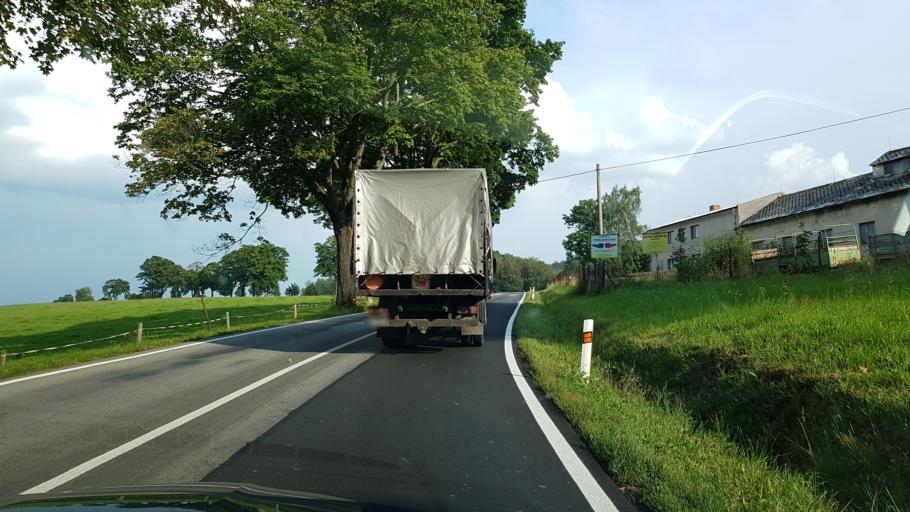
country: PL
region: Lower Silesian Voivodeship
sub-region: Powiat klodzki
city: Miedzylesie
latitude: 50.0991
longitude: 16.6354
